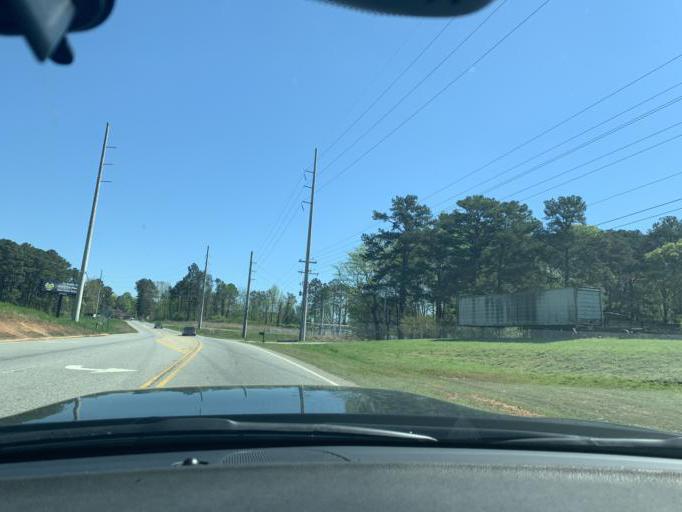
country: US
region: Georgia
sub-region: Forsyth County
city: Cumming
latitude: 34.1567
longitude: -84.1960
